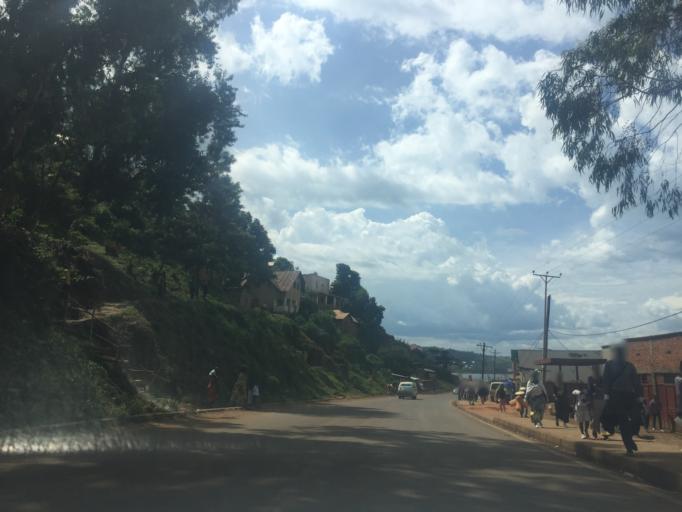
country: CD
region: South Kivu
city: Bukavu
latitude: -2.4871
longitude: 28.8466
